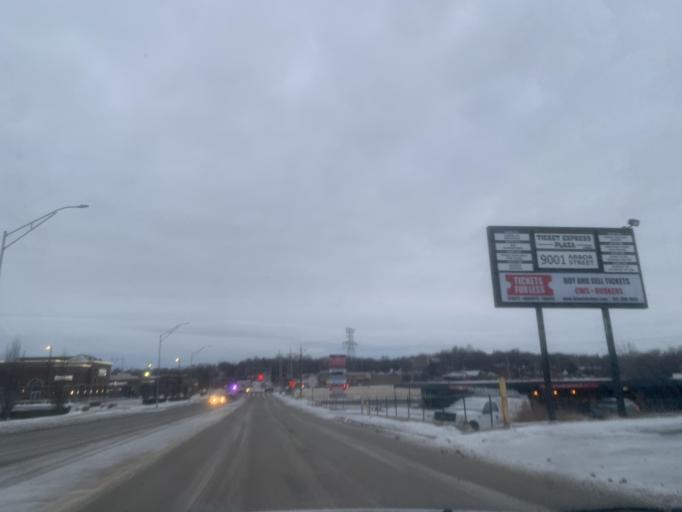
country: US
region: Nebraska
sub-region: Douglas County
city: Ralston
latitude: 41.2364
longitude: -96.0527
